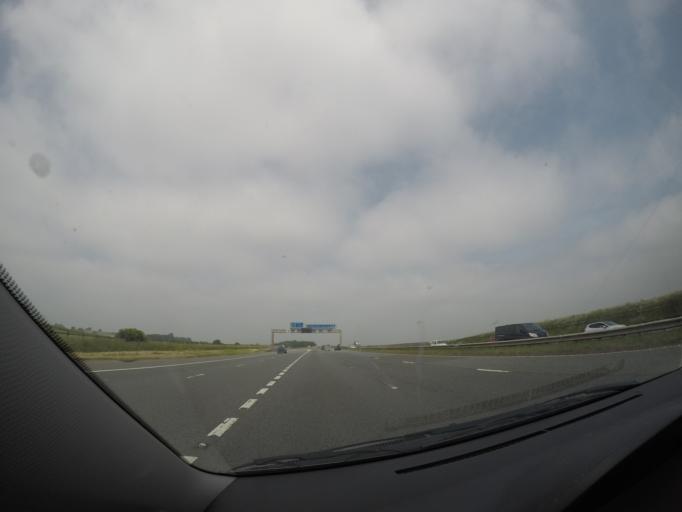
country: GB
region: England
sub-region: North Yorkshire
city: Boroughbridge
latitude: 54.1422
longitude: -1.4299
